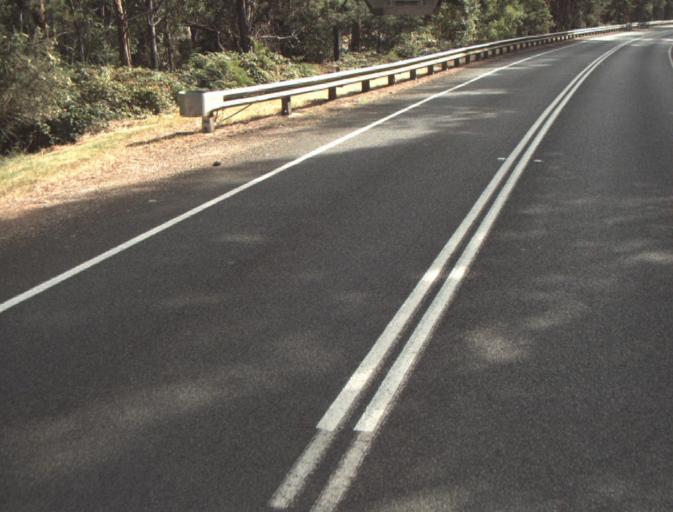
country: AU
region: Tasmania
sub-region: Launceston
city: Mayfield
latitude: -41.3004
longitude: 147.2070
